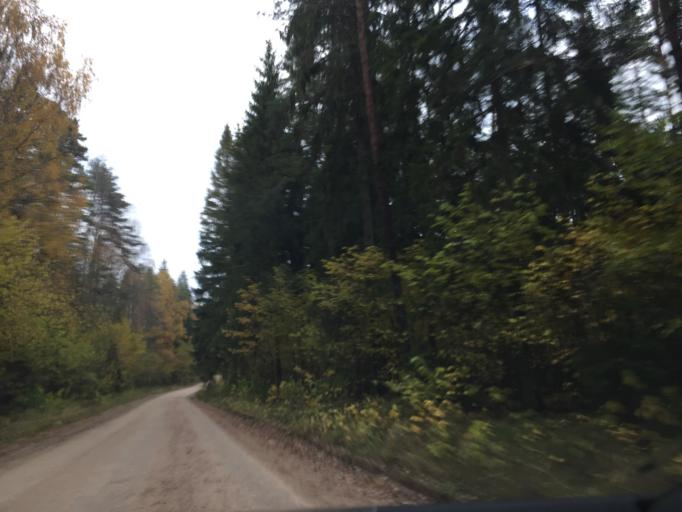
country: LV
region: Cesu Rajons
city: Cesis
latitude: 57.3520
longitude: 25.1662
